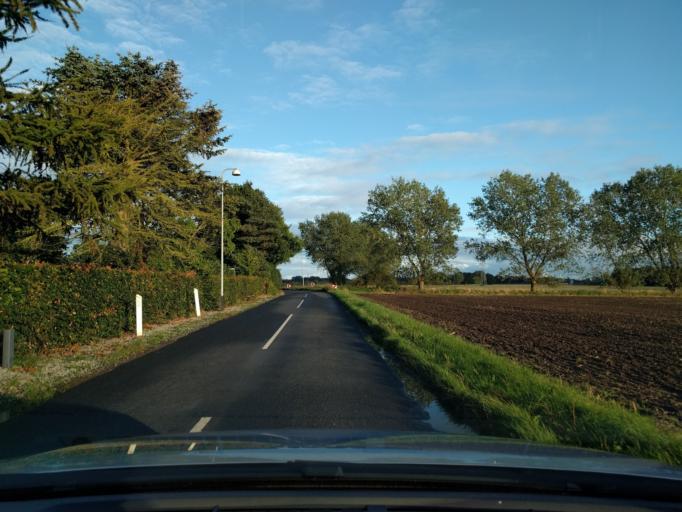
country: DK
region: South Denmark
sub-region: Odense Kommune
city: Bullerup
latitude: 55.4254
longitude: 10.4973
